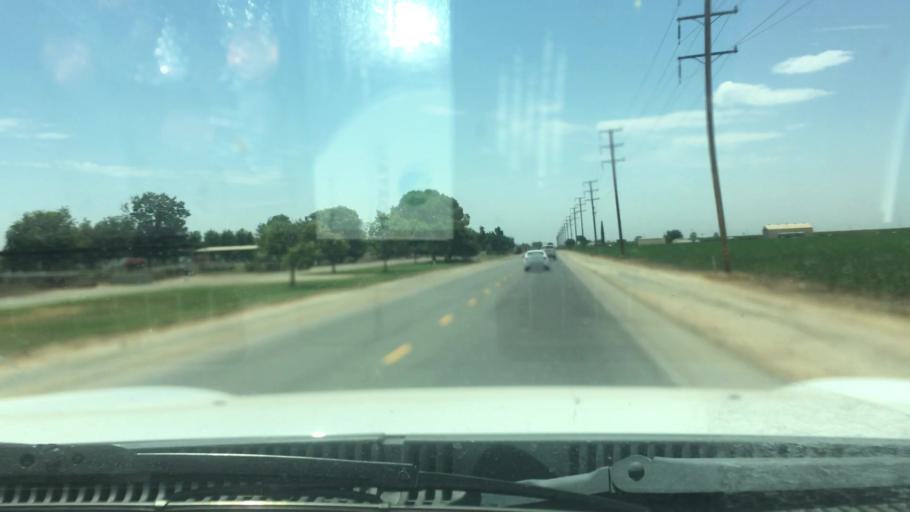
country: US
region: California
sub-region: Tulare County
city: Tipton
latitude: 36.0657
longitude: -119.2882
